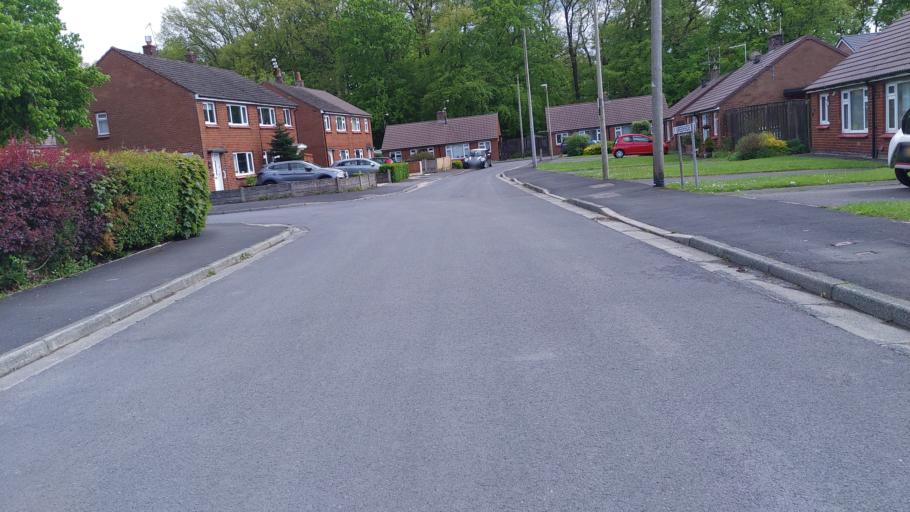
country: GB
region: England
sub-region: Lancashire
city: Euxton
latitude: 53.6672
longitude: -2.6800
